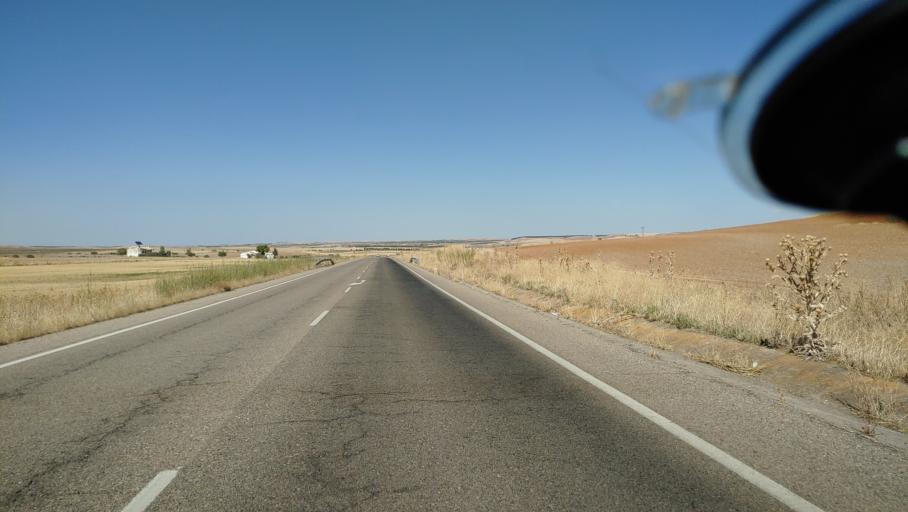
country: ES
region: Castille-La Mancha
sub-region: Province of Toledo
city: Pulgar
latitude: 39.7153
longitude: -4.1299
